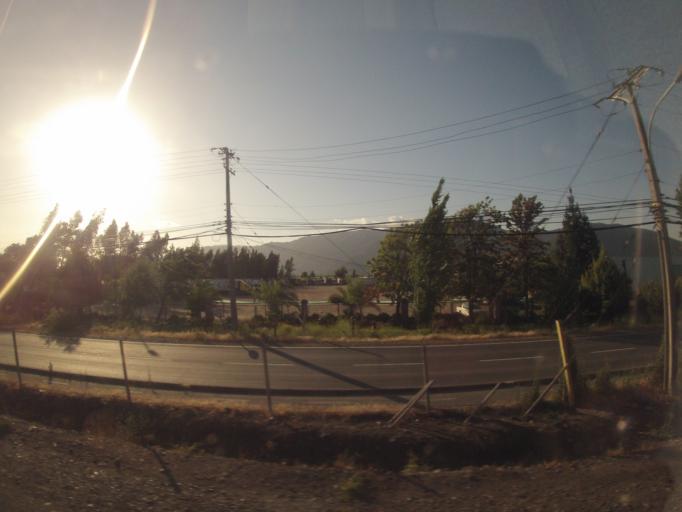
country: CL
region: O'Higgins
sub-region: Provincia de Colchagua
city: Chimbarongo
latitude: -34.5641
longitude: -70.9686
